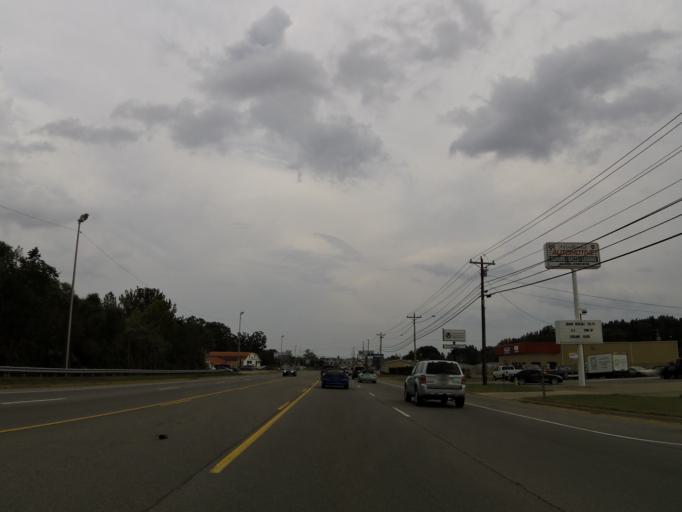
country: US
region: Tennessee
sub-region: Dickson County
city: Burns
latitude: 36.0305
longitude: -87.3489
